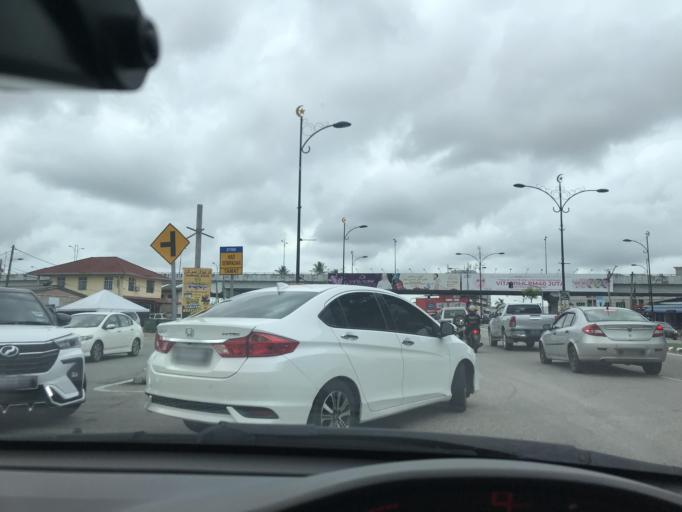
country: MY
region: Kelantan
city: Kota Bharu
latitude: 6.1150
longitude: 102.2369
